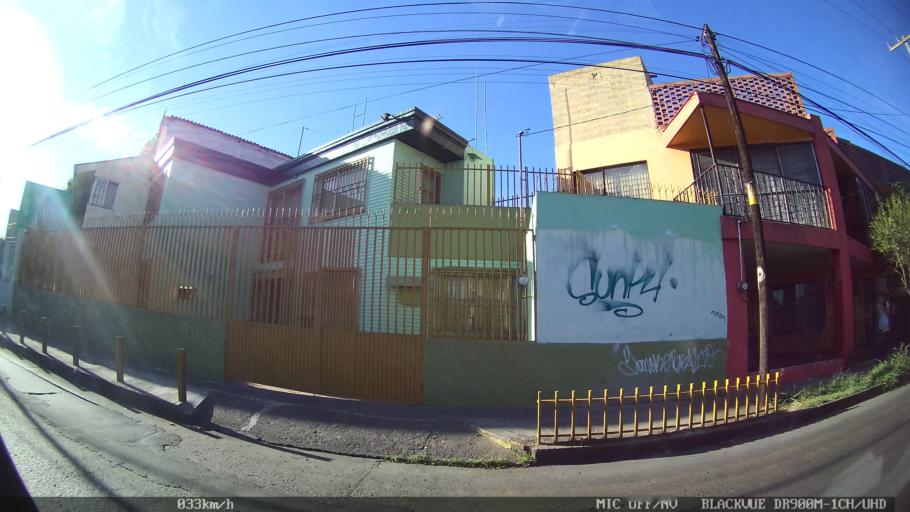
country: MX
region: Jalisco
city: Tlaquepaque
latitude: 20.6494
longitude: -103.3040
